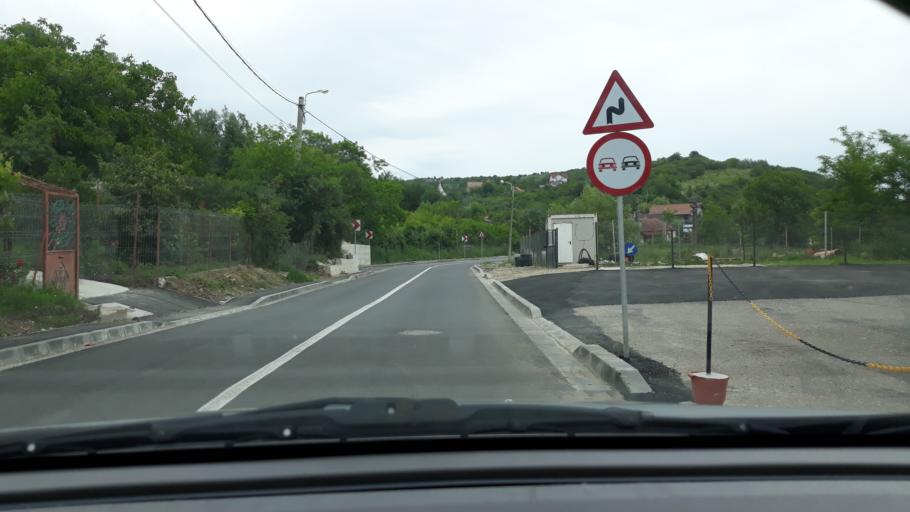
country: RO
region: Bihor
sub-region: Comuna Osorheiu
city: Alparea
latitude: 47.0596
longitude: 22.0025
